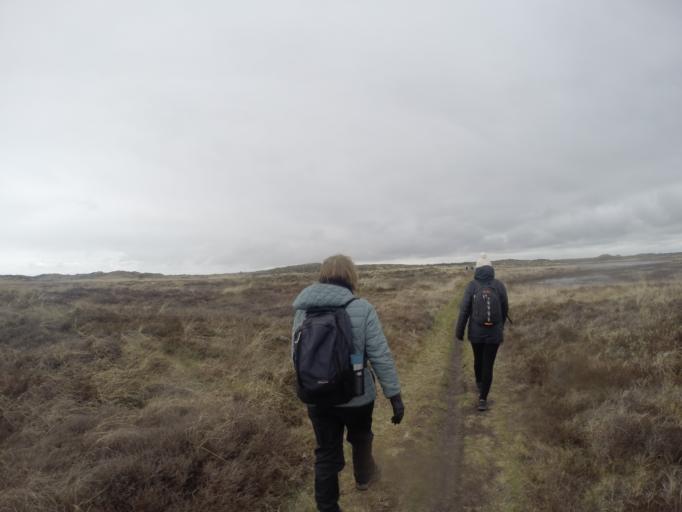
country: DK
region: North Denmark
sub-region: Thisted Kommune
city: Hurup
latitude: 56.8927
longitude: 8.3285
